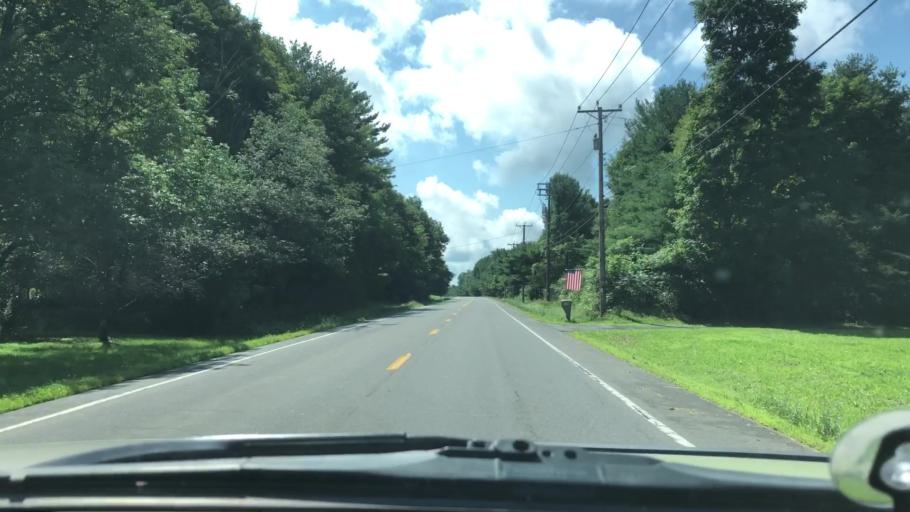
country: US
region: New York
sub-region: Greene County
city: Cairo
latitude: 42.2756
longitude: -73.9784
